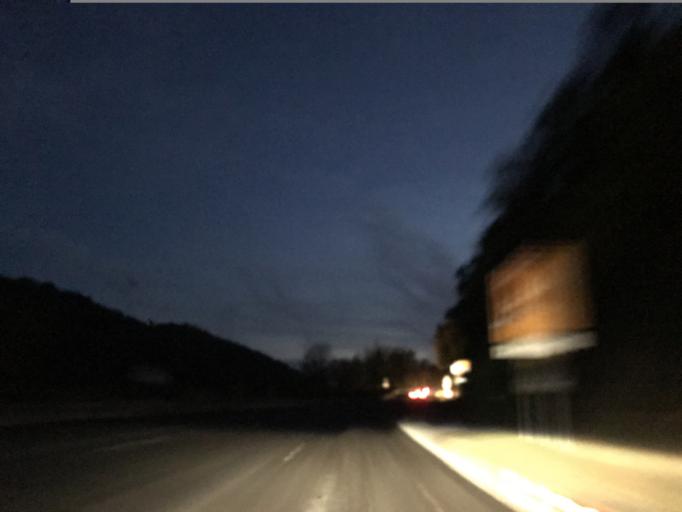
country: FR
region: Auvergne
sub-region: Departement du Puy-de-Dome
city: Thiers
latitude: 45.8649
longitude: 3.5613
